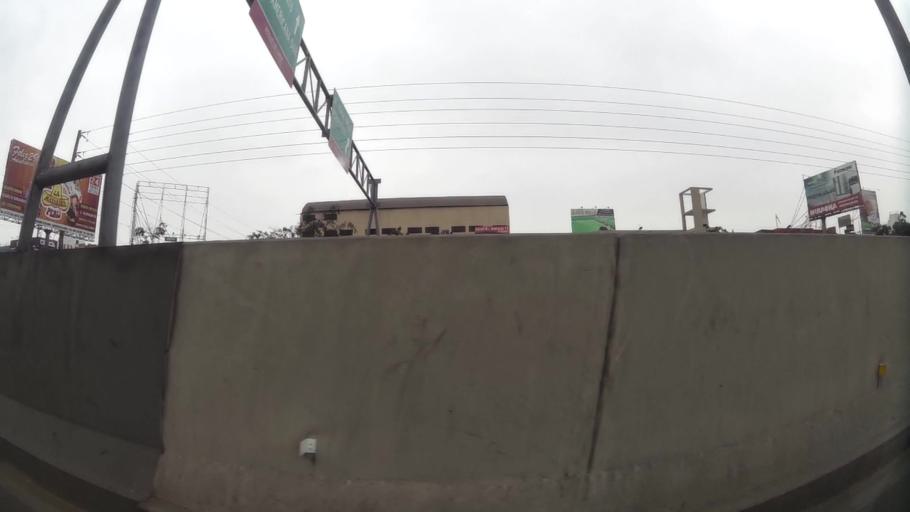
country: PE
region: Lima
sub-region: Lima
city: Independencia
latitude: -11.9952
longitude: -77.0633
